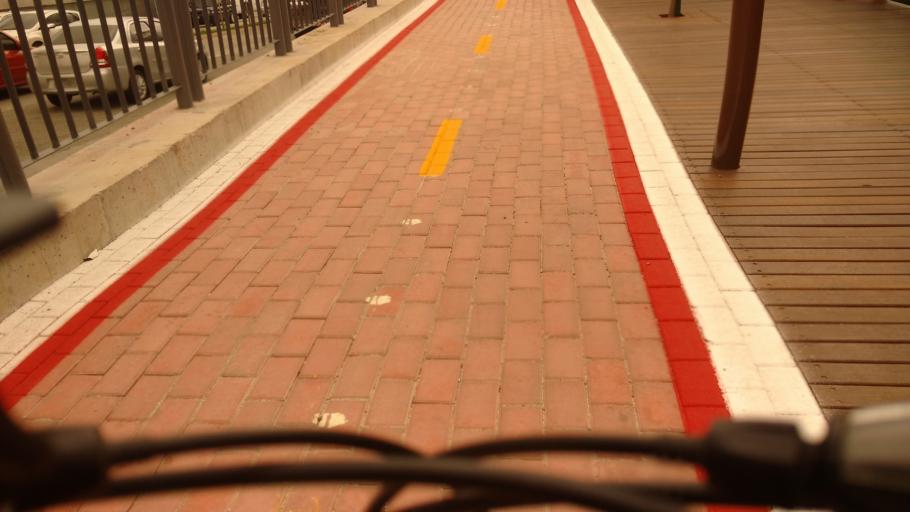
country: BR
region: Ceara
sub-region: Fortaleza
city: Fortaleza
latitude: -3.7448
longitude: -38.4886
